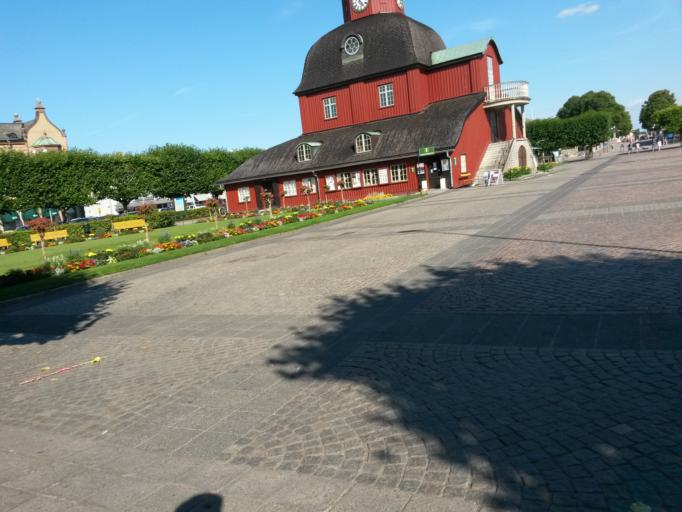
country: SE
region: Vaestra Goetaland
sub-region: Lidkopings Kommun
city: Lidkoping
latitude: 58.5040
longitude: 13.1568
